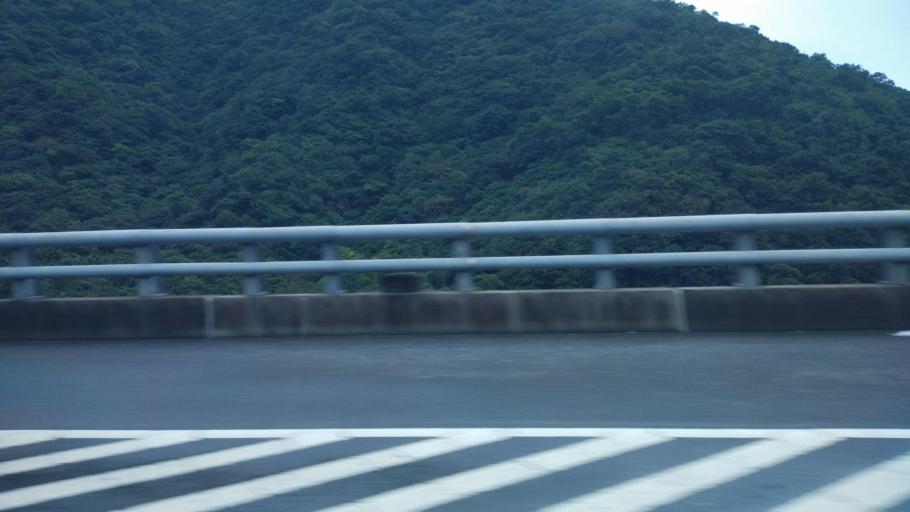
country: TW
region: Taiwan
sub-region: Yilan
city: Yilan
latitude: 24.5305
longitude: 121.8334
